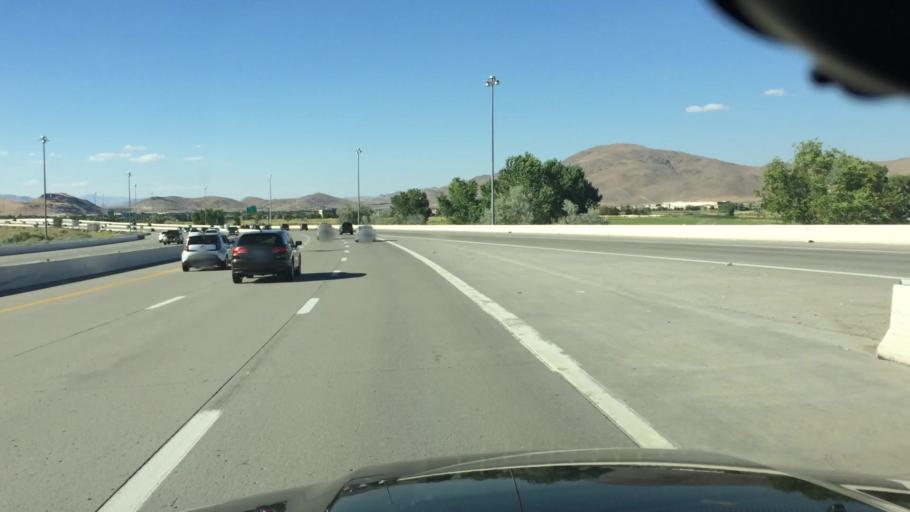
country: US
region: Nevada
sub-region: Washoe County
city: Sparks
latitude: 39.4125
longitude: -119.7474
